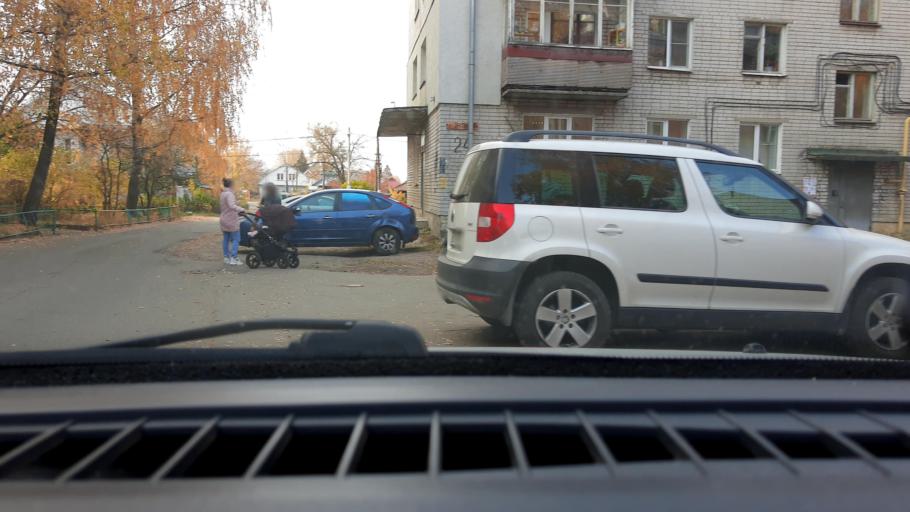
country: RU
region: Nizjnij Novgorod
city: Gorbatovka
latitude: 56.3589
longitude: 43.8429
